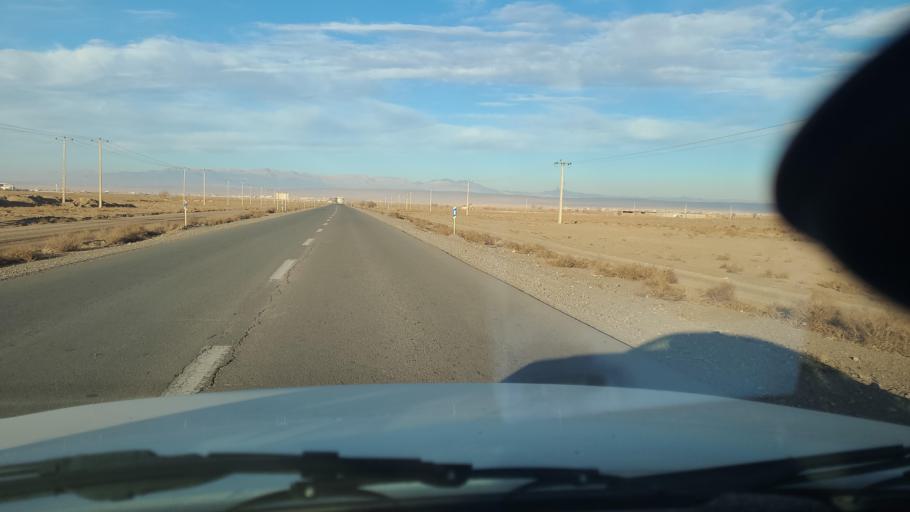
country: IR
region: Razavi Khorasan
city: Neqab
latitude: 36.5918
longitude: 57.5853
